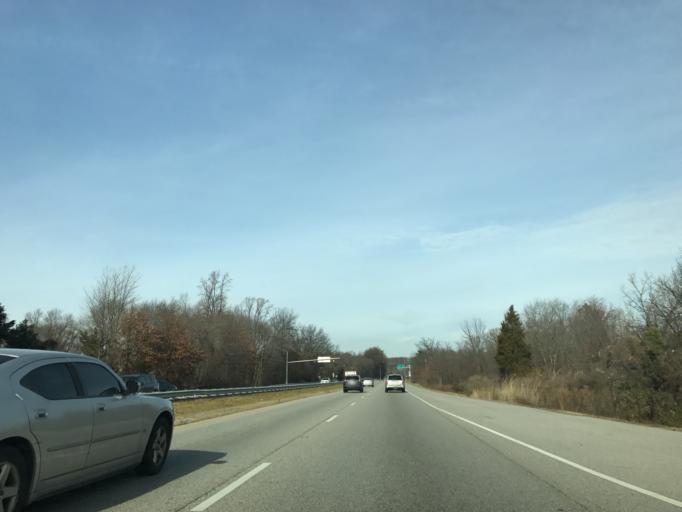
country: US
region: Maryland
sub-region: Baltimore County
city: Parkville
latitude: 39.3904
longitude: -76.5507
